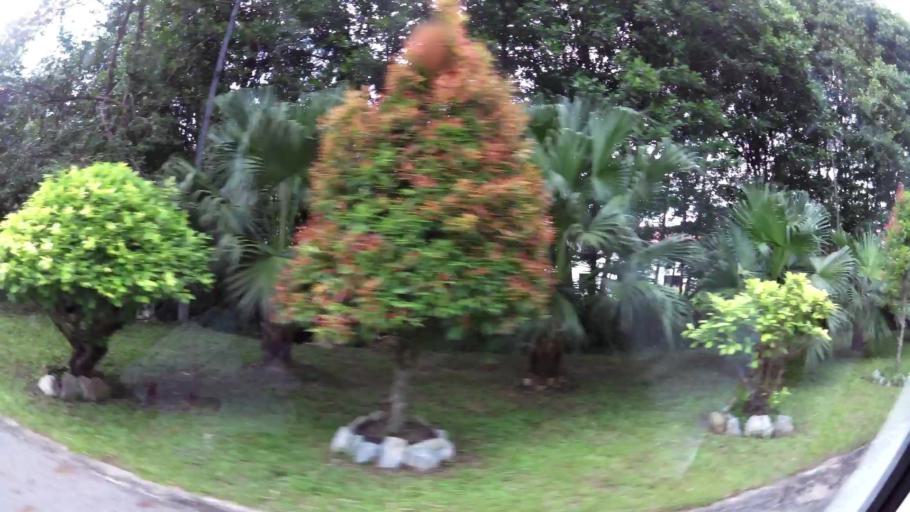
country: BN
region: Brunei and Muara
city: Bandar Seri Begawan
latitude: 4.9124
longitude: 115.0032
